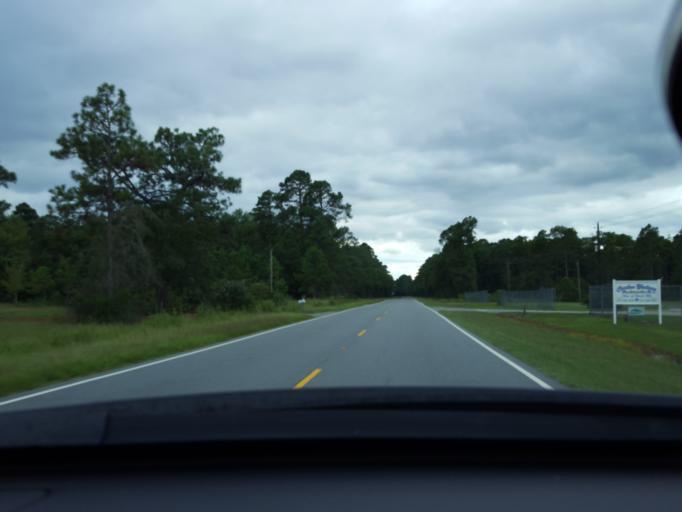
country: US
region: North Carolina
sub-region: Bladen County
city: Elizabethtown
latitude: 34.7073
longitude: -78.4651
